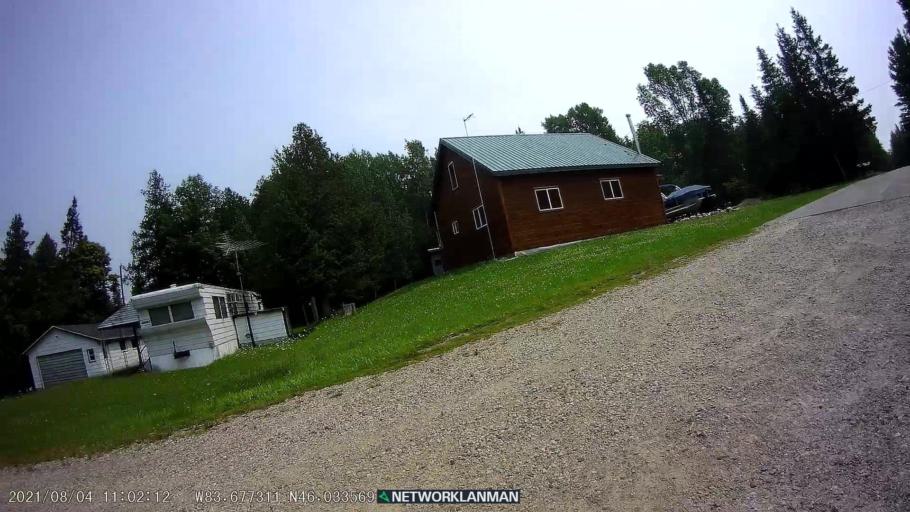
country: CA
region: Ontario
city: Thessalon
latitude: 46.0335
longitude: -83.6773
